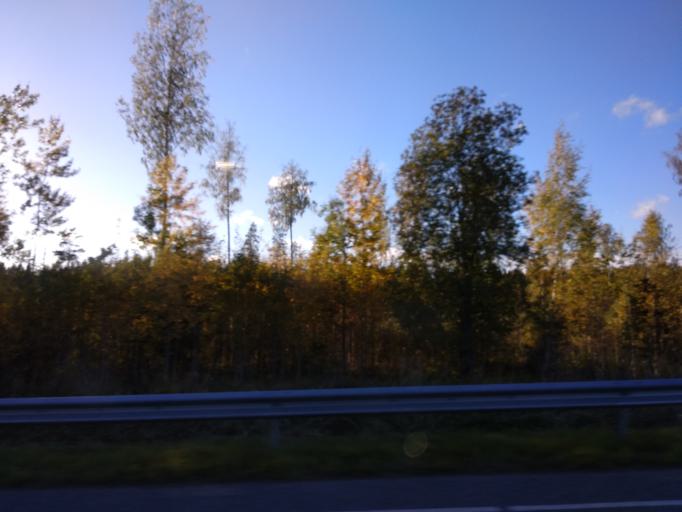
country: EE
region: Polvamaa
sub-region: Polva linn
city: Polva
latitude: 58.0268
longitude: 27.0647
